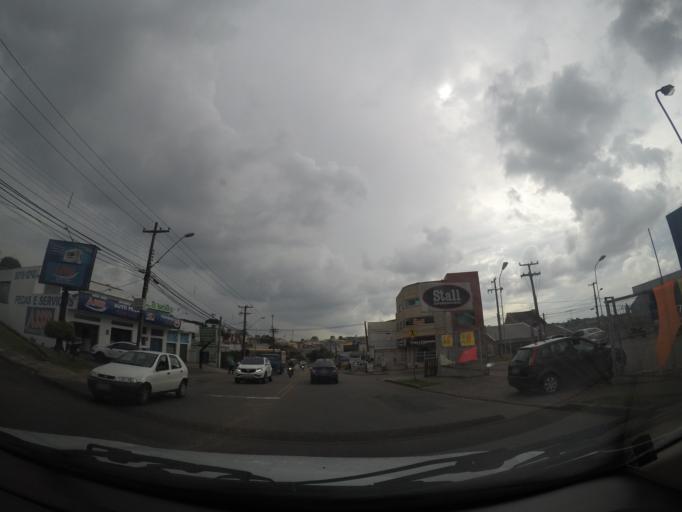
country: BR
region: Parana
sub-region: Sao Jose Dos Pinhais
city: Sao Jose dos Pinhais
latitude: -25.5275
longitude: -49.2504
